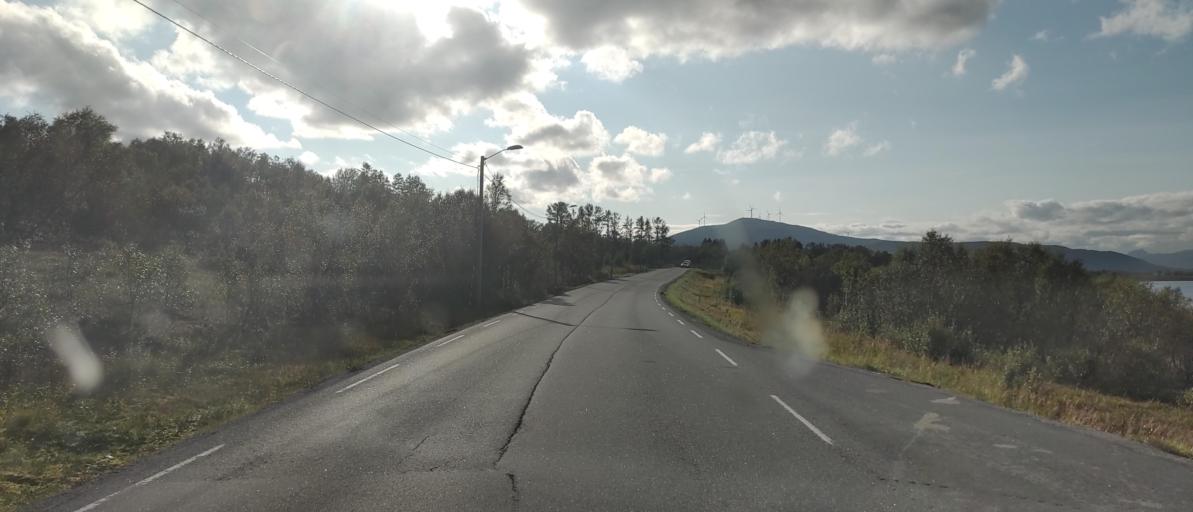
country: NO
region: Nordland
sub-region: Sortland
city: Sortland
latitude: 68.7211
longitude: 15.5137
